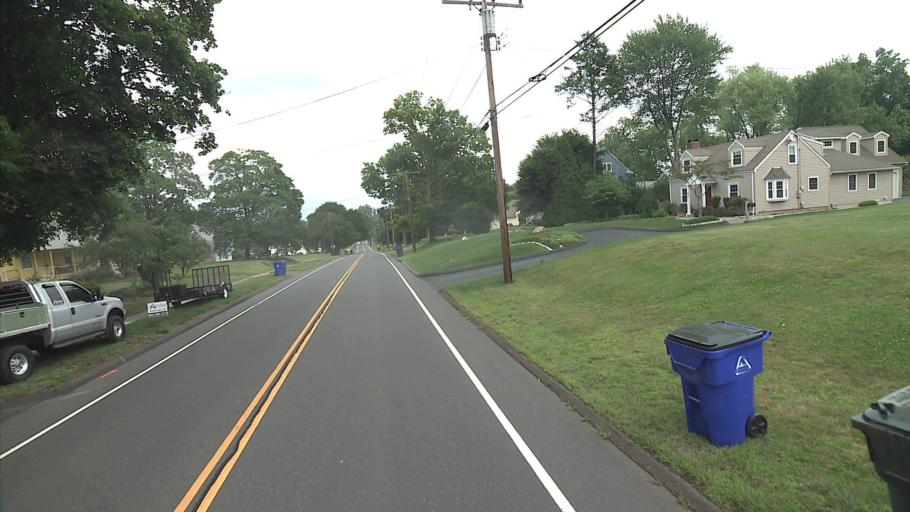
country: US
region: Connecticut
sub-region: Hartford County
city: Wethersfield
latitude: 41.6924
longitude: -72.6772
